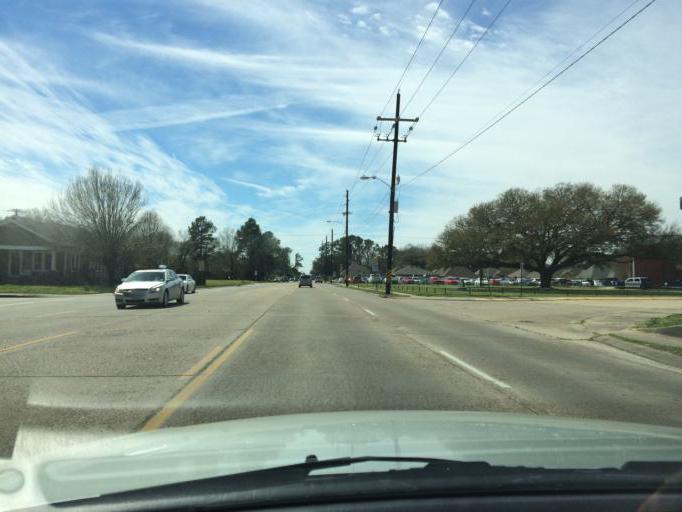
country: US
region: Louisiana
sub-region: Lafayette Parish
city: Lafayette
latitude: 30.2070
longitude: -92.0571
